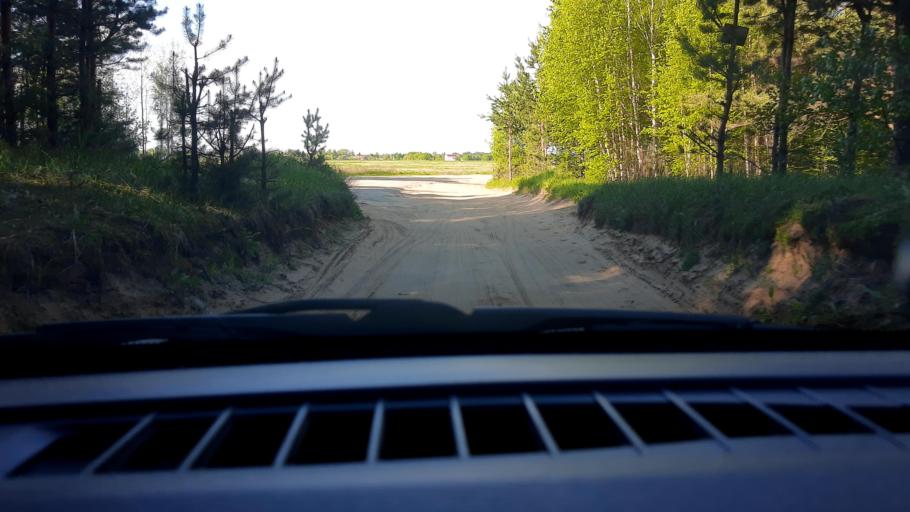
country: RU
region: Nizjnij Novgorod
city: Sitniki
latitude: 56.4140
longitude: 44.0610
